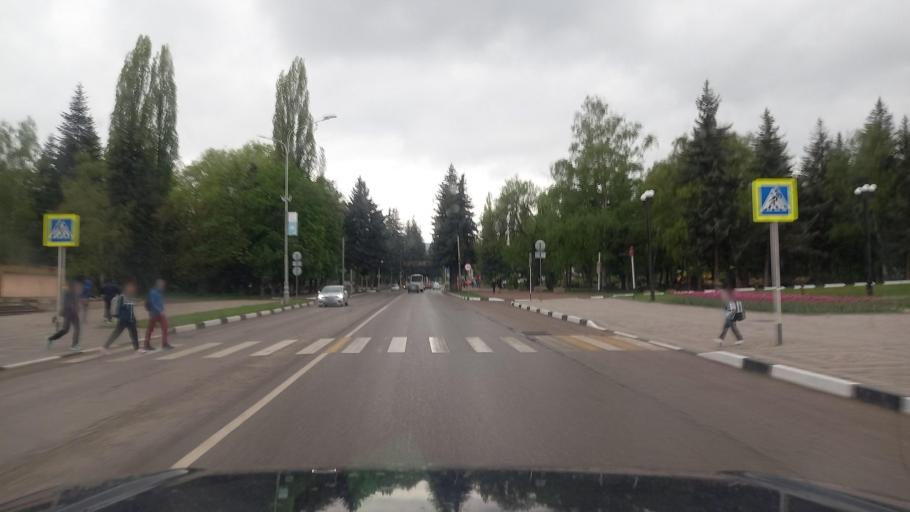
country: RU
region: Stavropol'skiy
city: Kislovodsk
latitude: 43.9125
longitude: 42.7185
